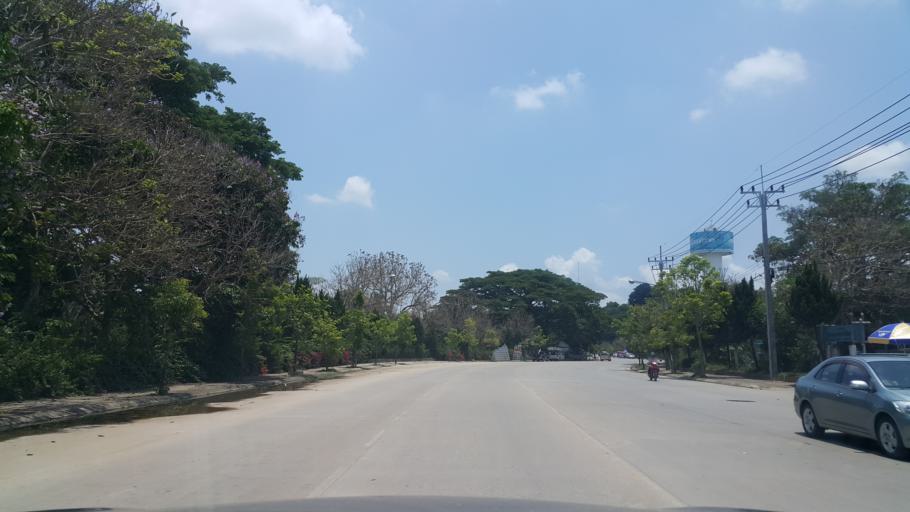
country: TH
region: Chiang Rai
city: Chiang Rai
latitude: 19.9200
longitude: 99.8215
